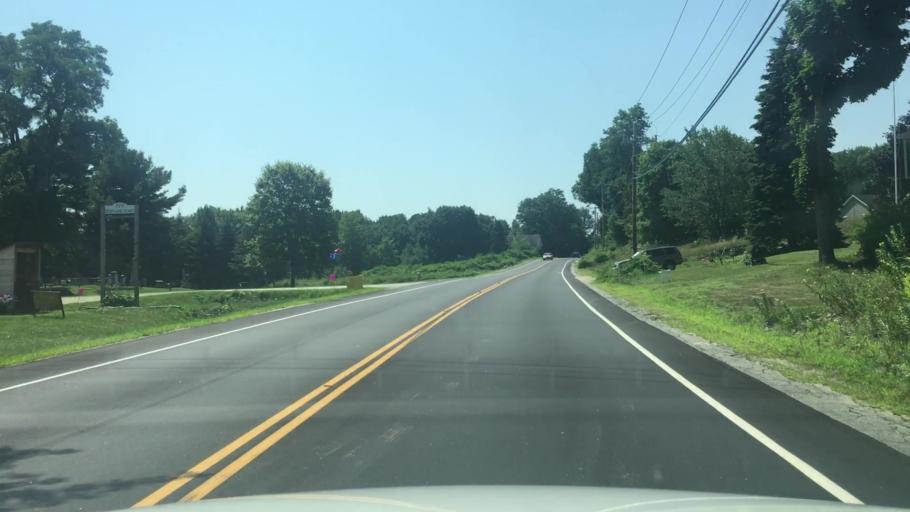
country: US
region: Maine
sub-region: Cumberland County
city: Cumberland Center
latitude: 43.8560
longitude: -70.3211
